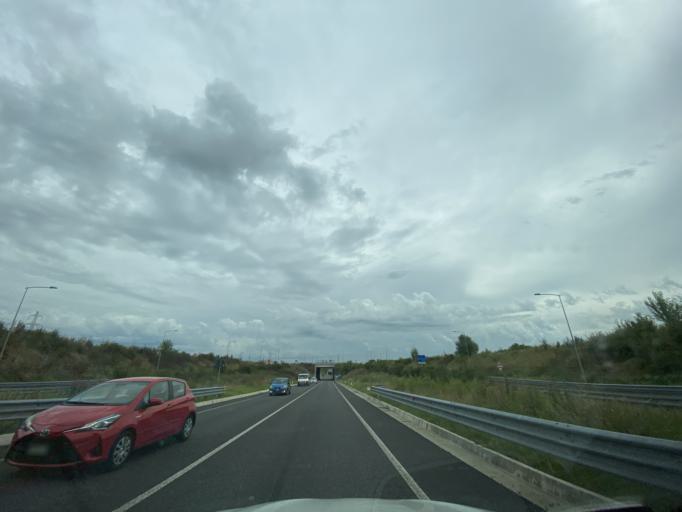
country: IT
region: Lombardy
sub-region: Citta metropolitana di Milano
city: Pessano Con Bornago
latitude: 45.5597
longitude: 9.3841
